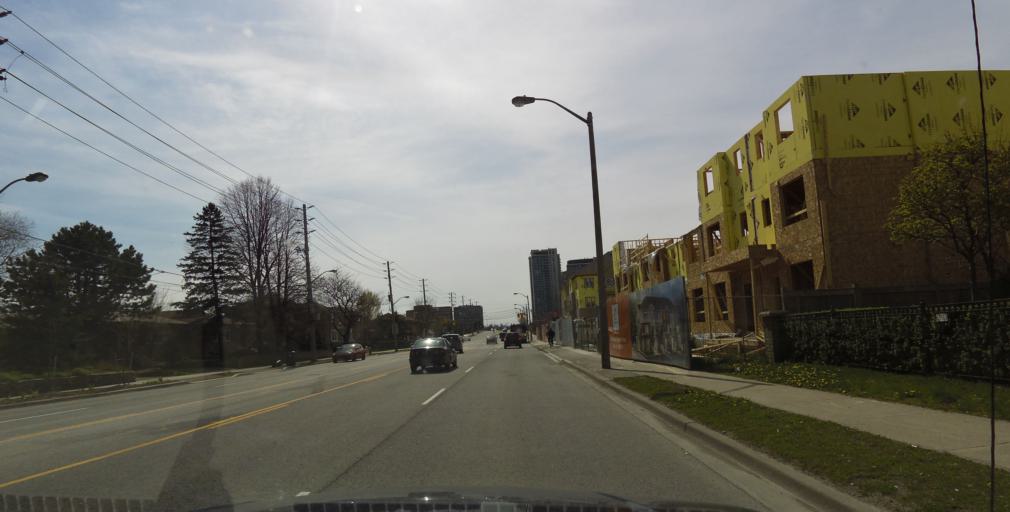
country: CA
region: Ontario
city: Etobicoke
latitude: 43.6104
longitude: -79.5507
